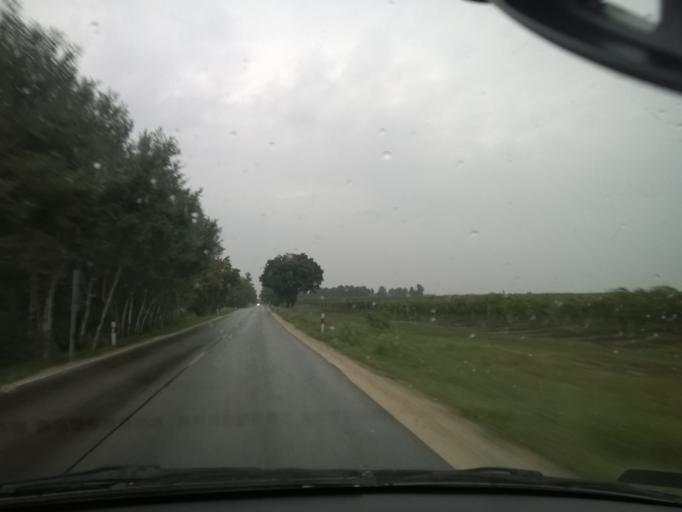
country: HU
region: Pest
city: Domsod
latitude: 47.0618
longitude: 19.0165
